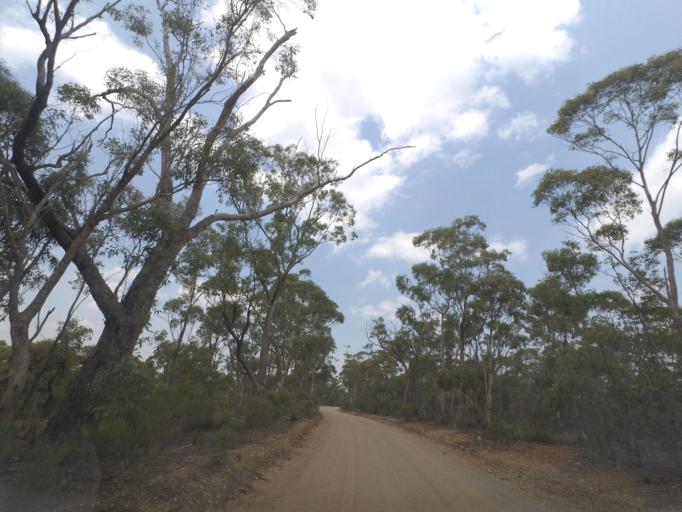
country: AU
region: Victoria
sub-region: Moorabool
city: Bacchus Marsh
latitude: -37.5988
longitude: 144.4458
